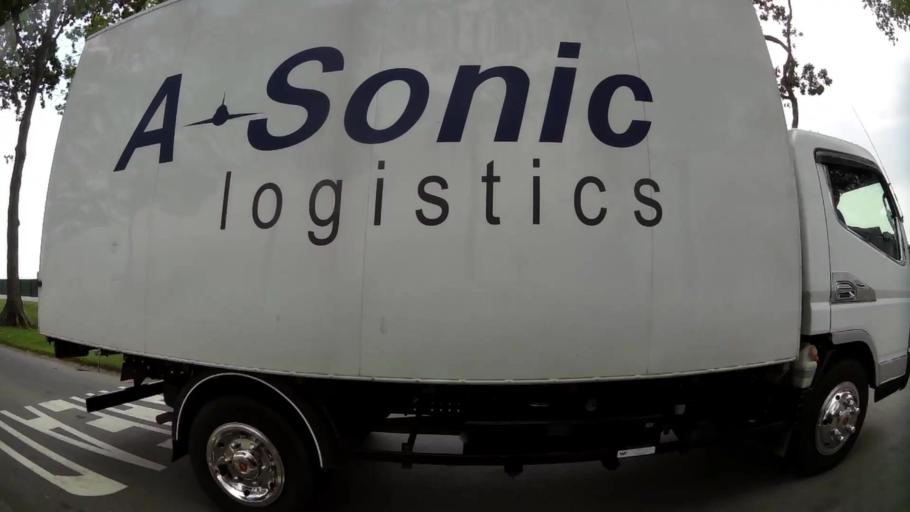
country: SG
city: Singapore
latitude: 1.3396
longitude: 103.9925
